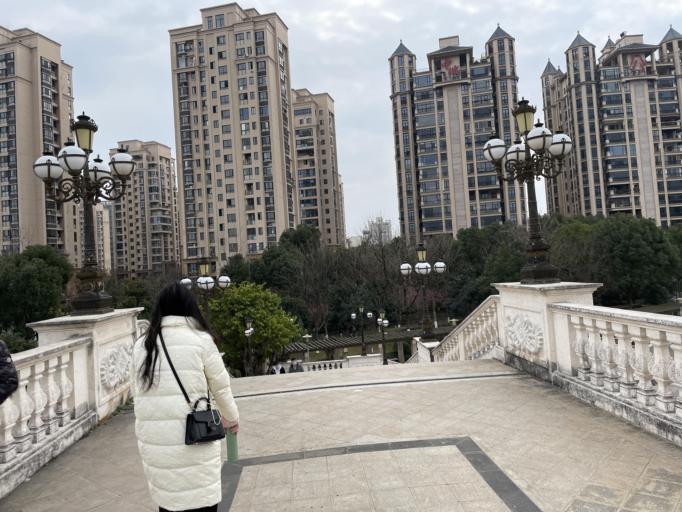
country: CN
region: Zhejiang Sheng
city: Wenzhou
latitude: 27.9974
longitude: 120.6631
